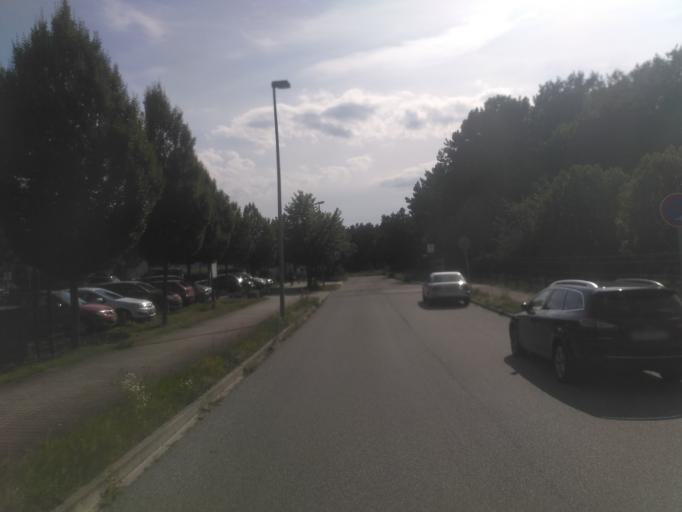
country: DE
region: Saxony
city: Hoyerswerda
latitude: 51.4570
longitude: 14.2622
